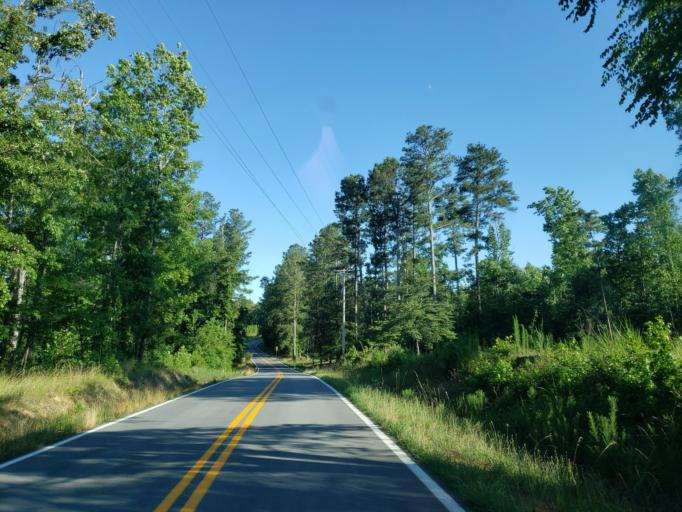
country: US
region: Georgia
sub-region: Floyd County
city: Shannon
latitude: 34.4522
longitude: -85.1142
